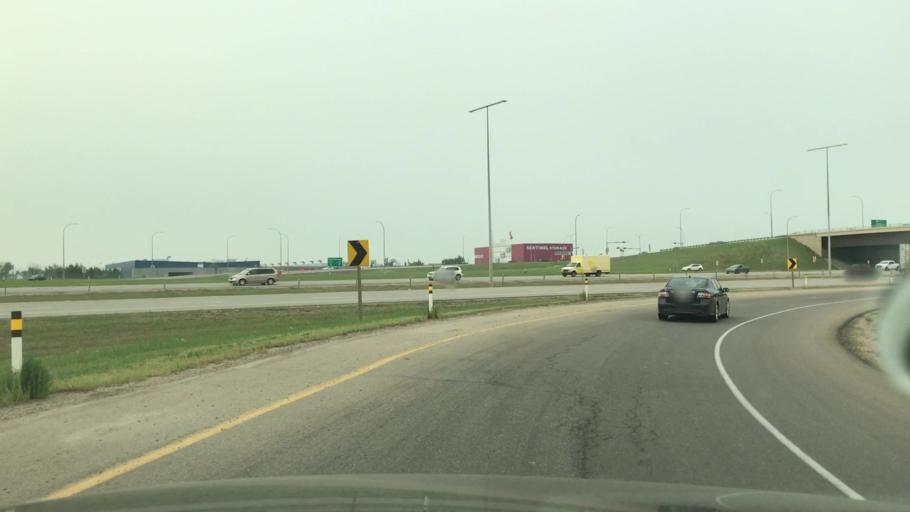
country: CA
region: Alberta
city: Edmonton
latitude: 53.4305
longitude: -113.5795
